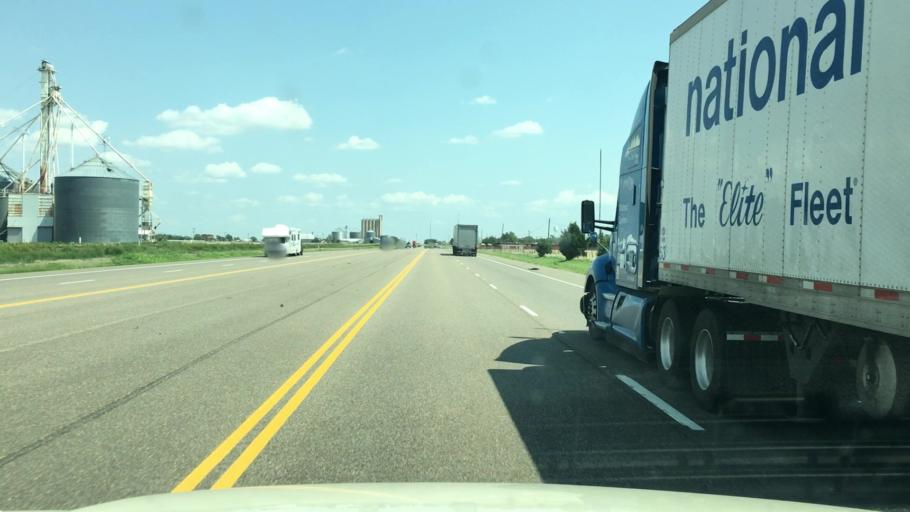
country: US
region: Texas
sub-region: Armstrong County
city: Claude
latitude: 35.1172
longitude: -101.3753
